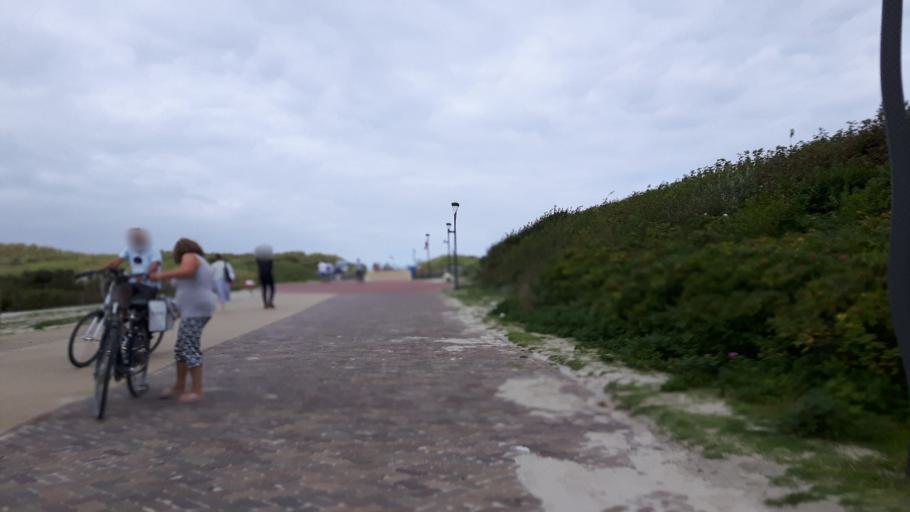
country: NL
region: Friesland
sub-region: Gemeente Ameland
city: Nes
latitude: 53.4584
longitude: 5.7775
